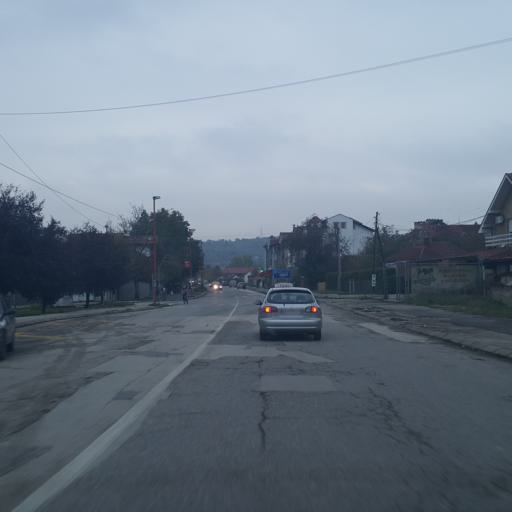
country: RS
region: Central Serbia
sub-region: Zajecarski Okrug
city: Zajecar
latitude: 43.9058
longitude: 22.2639
